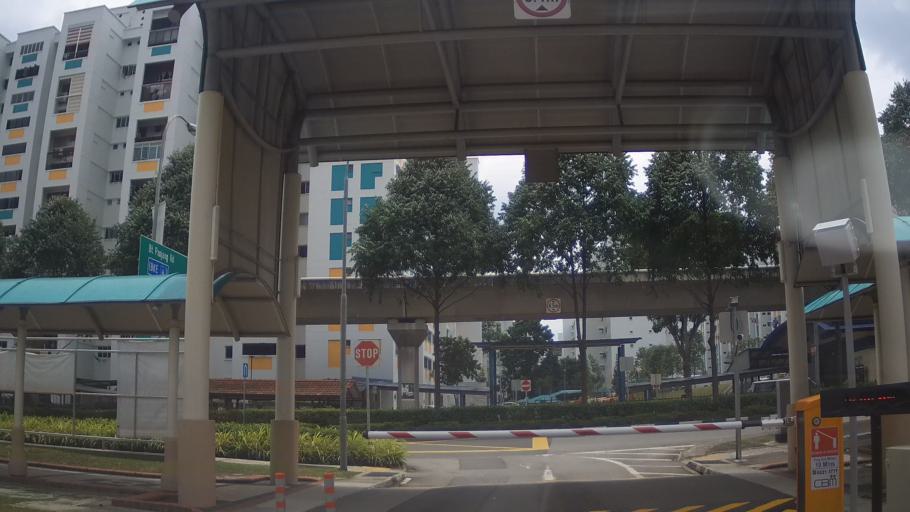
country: MY
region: Johor
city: Johor Bahru
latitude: 1.3767
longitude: 103.7710
